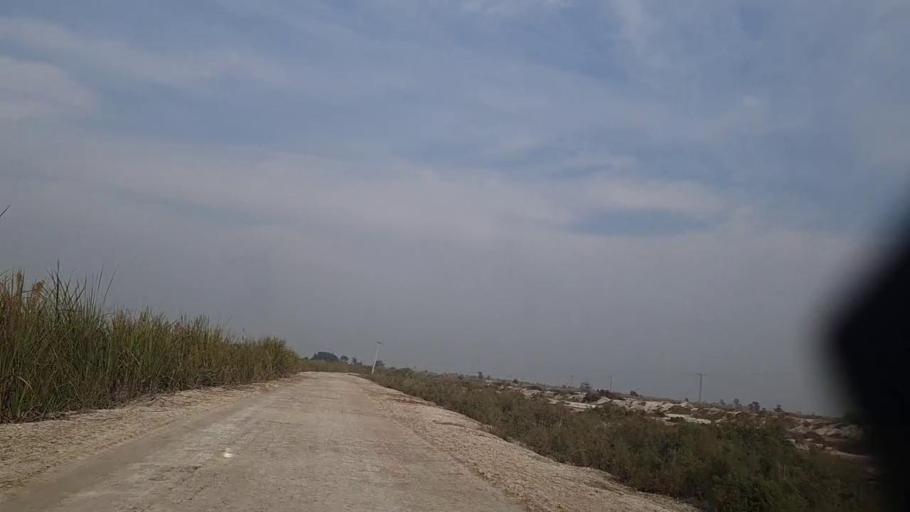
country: PK
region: Sindh
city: Daur
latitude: 26.3691
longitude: 68.2399
